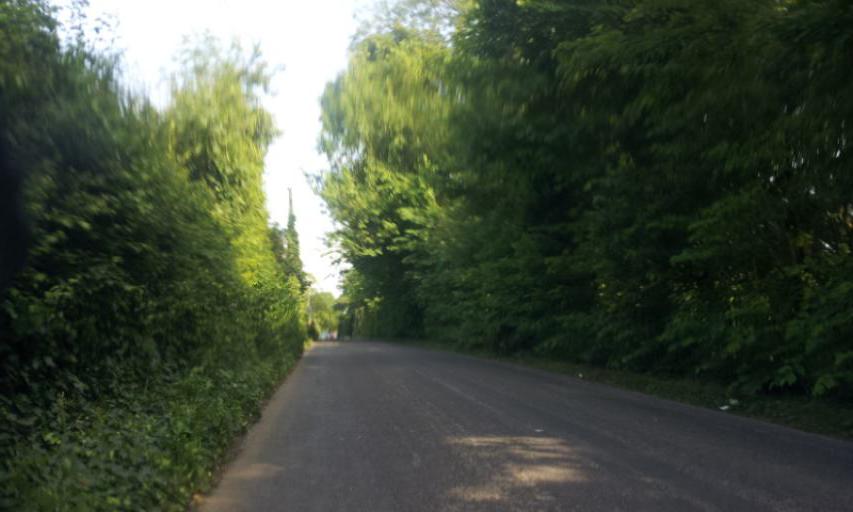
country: GB
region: England
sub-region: Kent
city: Lenham
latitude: 51.2400
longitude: 0.7105
